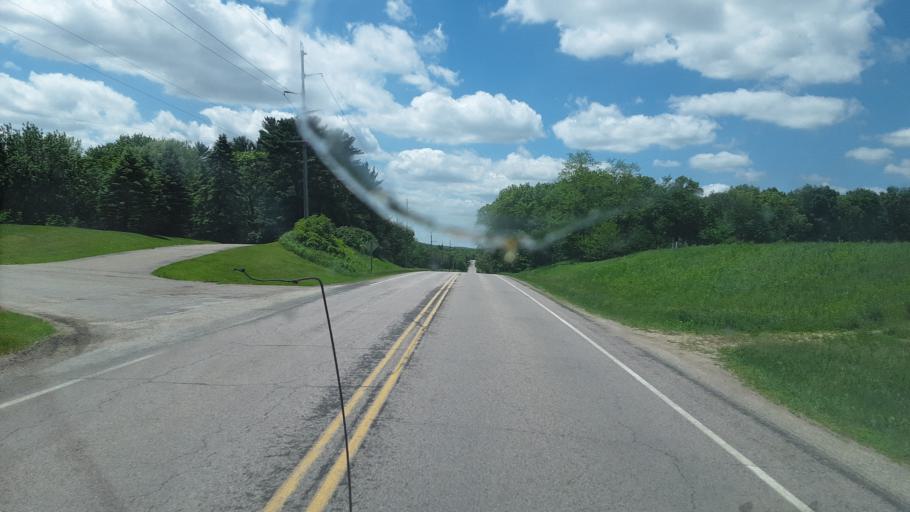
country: US
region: Wisconsin
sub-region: Sauk County
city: Lake Delton
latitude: 43.5910
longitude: -89.8731
